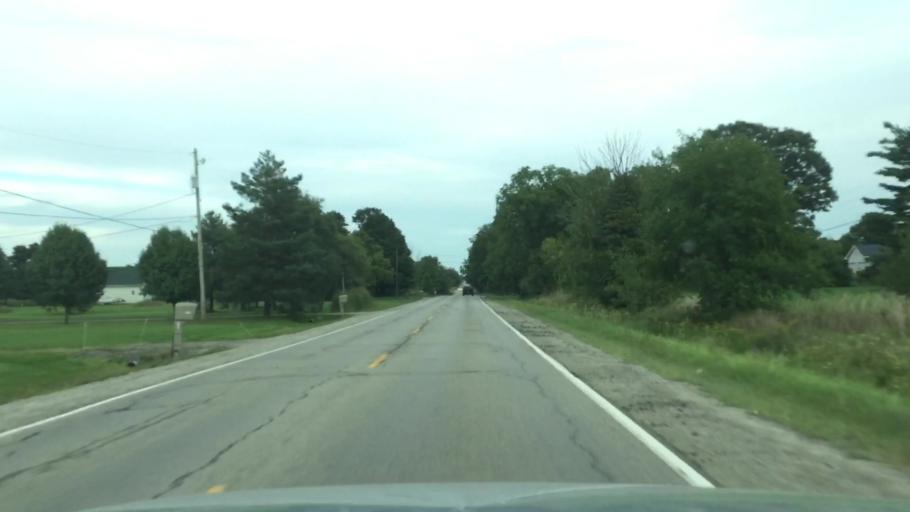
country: US
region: Michigan
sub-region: Genesee County
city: Lake Fenton
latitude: 42.8848
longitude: -83.7630
